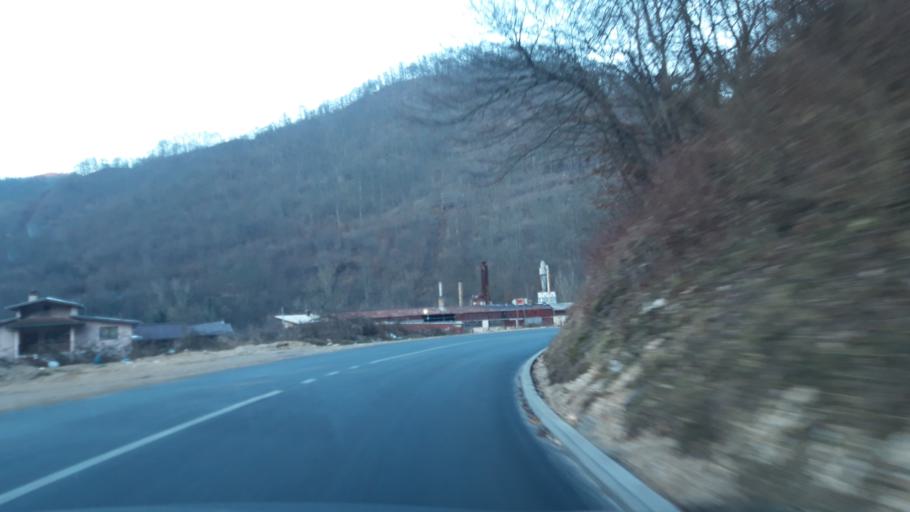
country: RS
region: Central Serbia
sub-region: Macvanski Okrug
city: Mali Zvornik
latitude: 44.2775
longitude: 19.1089
